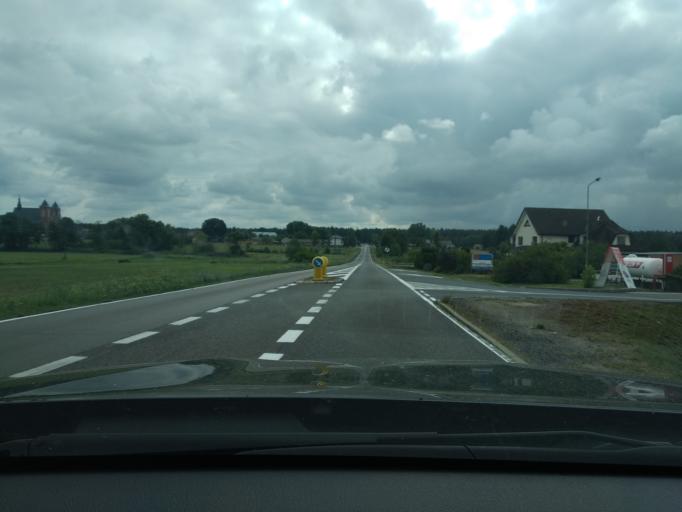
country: PL
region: Masovian Voivodeship
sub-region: Powiat pultuski
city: Obryte
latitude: 52.6498
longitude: 21.2451
